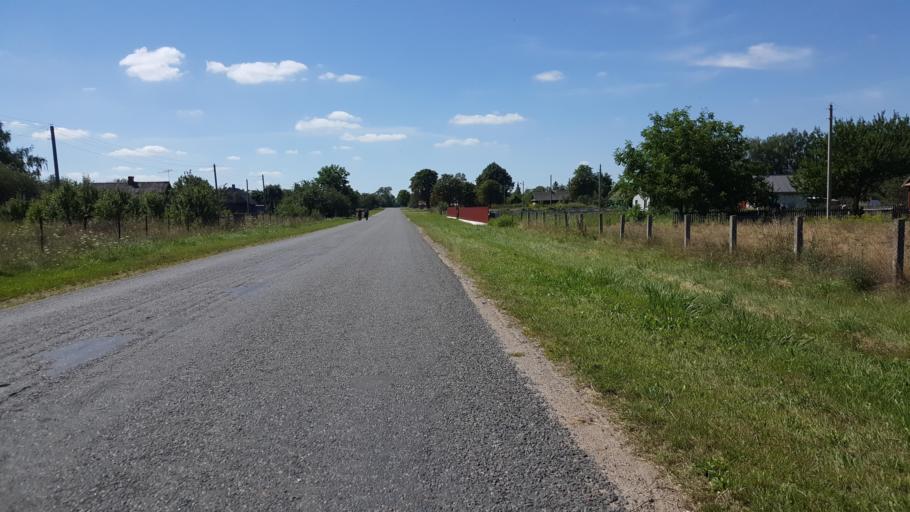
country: BY
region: Brest
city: Kamyanyets
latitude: 52.3708
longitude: 23.6283
